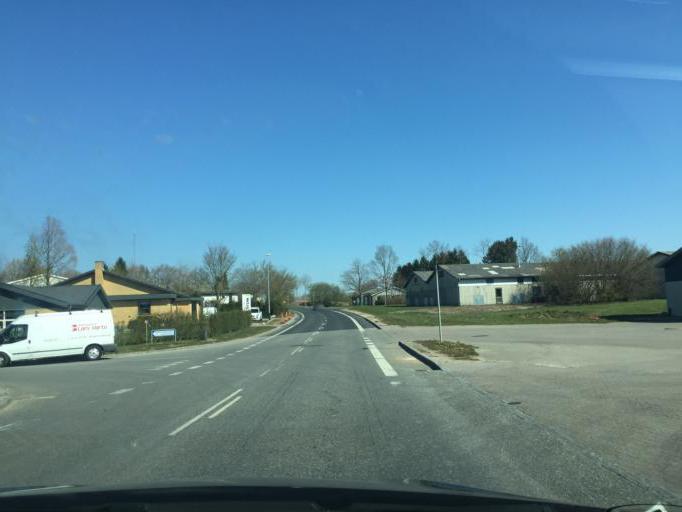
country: DK
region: South Denmark
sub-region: Faaborg-Midtfyn Kommune
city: Ringe
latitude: 55.2457
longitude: 10.4853
